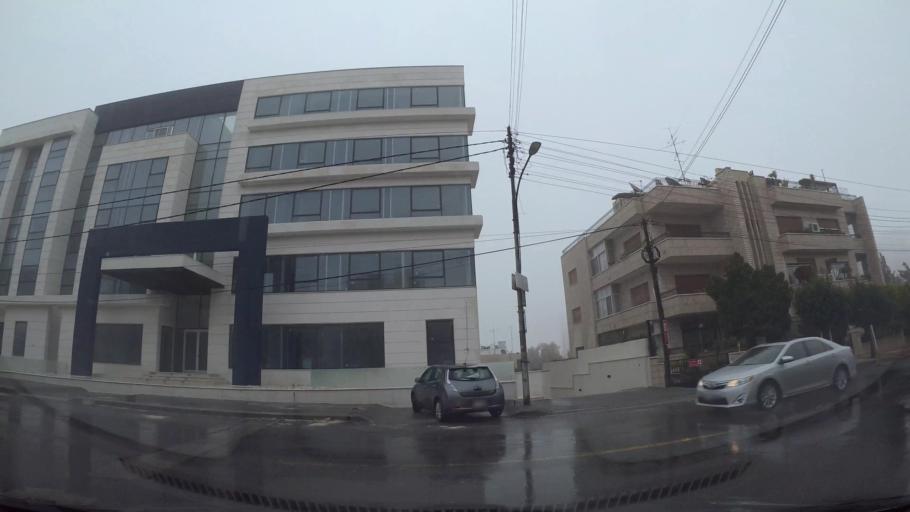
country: JO
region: Amman
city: Wadi as Sir
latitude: 31.9627
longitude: 35.8782
